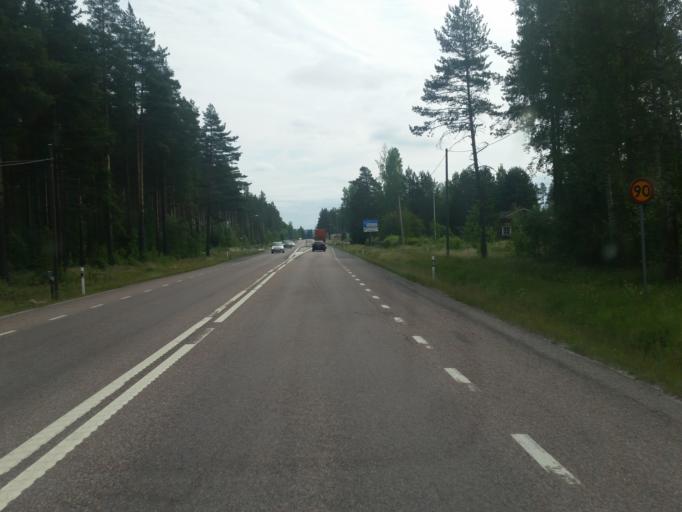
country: SE
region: Dalarna
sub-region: Borlange Kommun
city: Borlaenge
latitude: 60.5302
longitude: 15.3166
